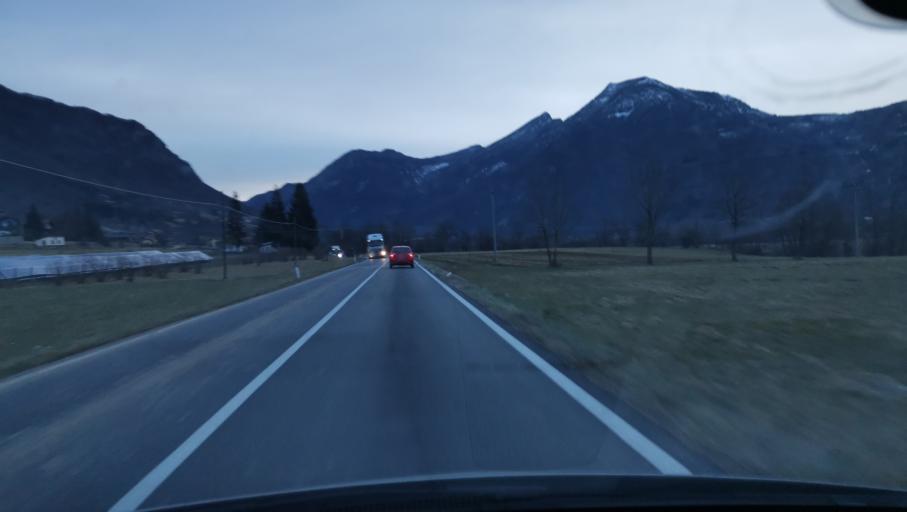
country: IT
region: Piedmont
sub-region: Provincia di Cuneo
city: Demonte
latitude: 44.3141
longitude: 7.3307
